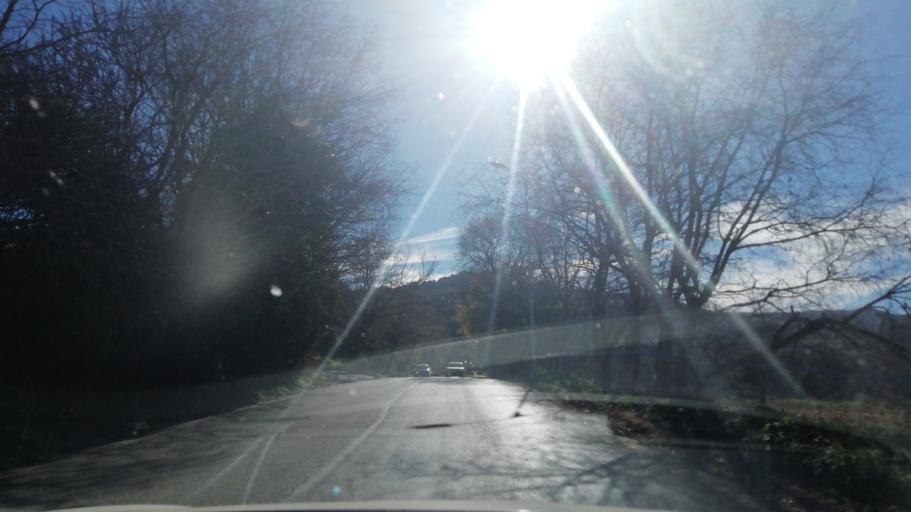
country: DZ
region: Tlemcen
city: Mansoura
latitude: 34.8666
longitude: -1.3330
